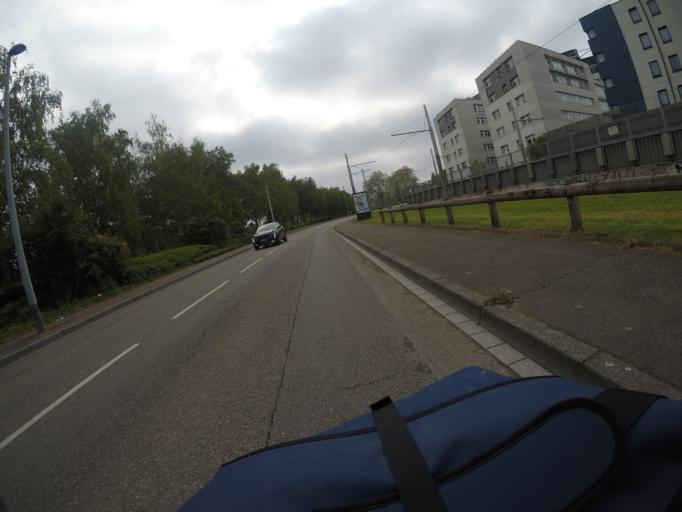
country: FR
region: Alsace
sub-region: Departement du Bas-Rhin
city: Strasbourg
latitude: 48.5915
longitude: 7.7273
